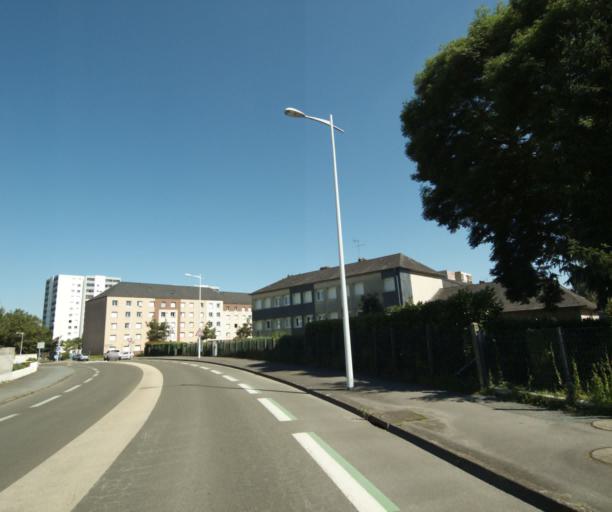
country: FR
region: Pays de la Loire
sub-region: Departement de la Mayenne
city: Laval
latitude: 48.0609
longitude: -0.7483
